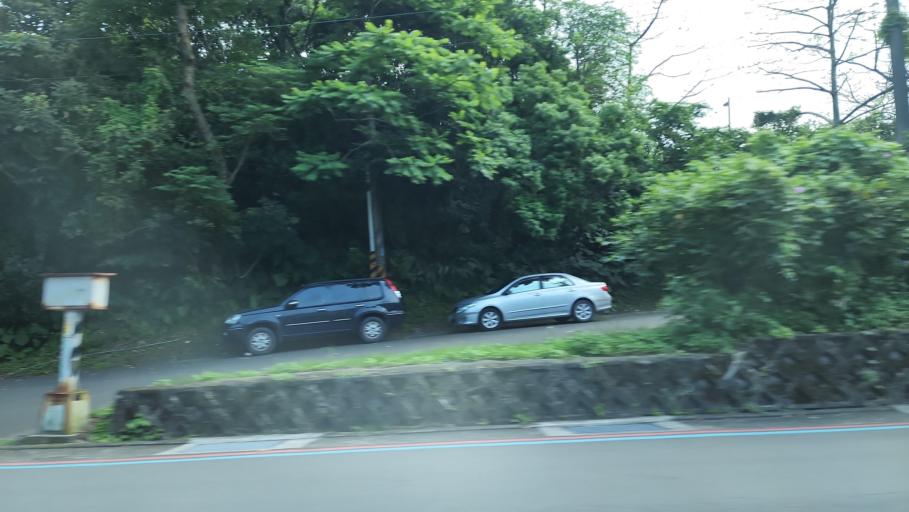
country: TW
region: Taiwan
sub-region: Keelung
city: Keelung
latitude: 25.2230
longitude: 121.6445
